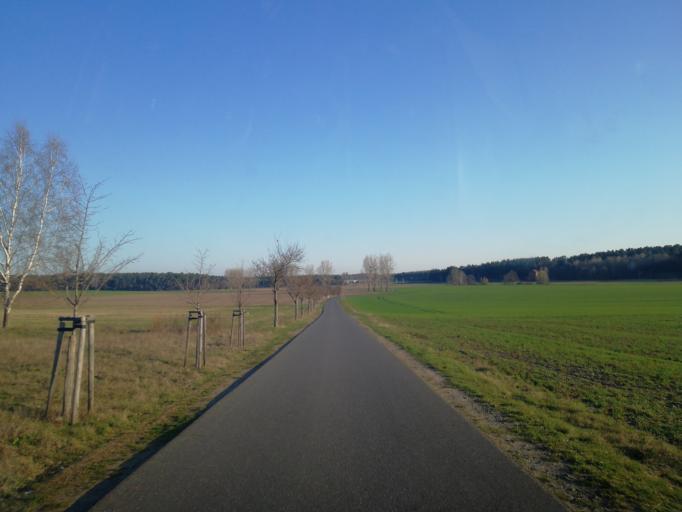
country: DE
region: Brandenburg
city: Drahnsdorf
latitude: 51.8816
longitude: 13.5838
